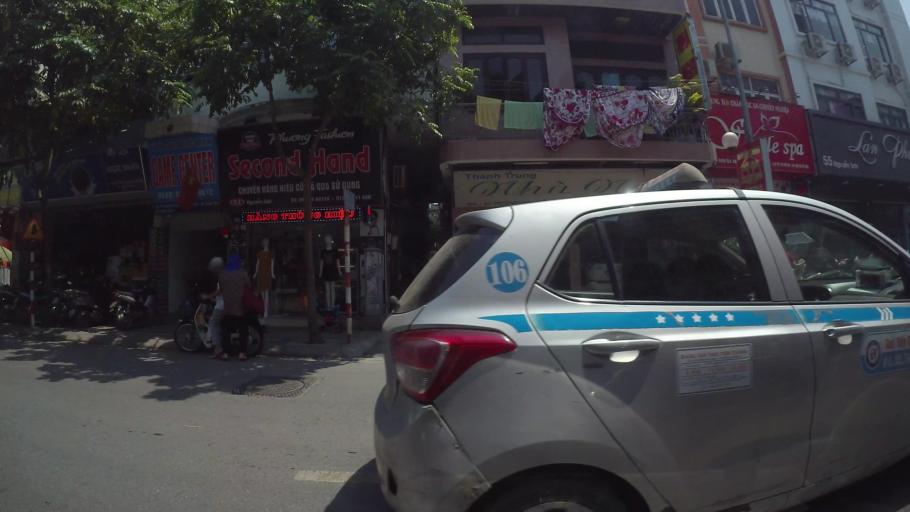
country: VN
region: Ha Noi
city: Hoan Kiem
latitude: 21.0473
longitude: 105.8774
